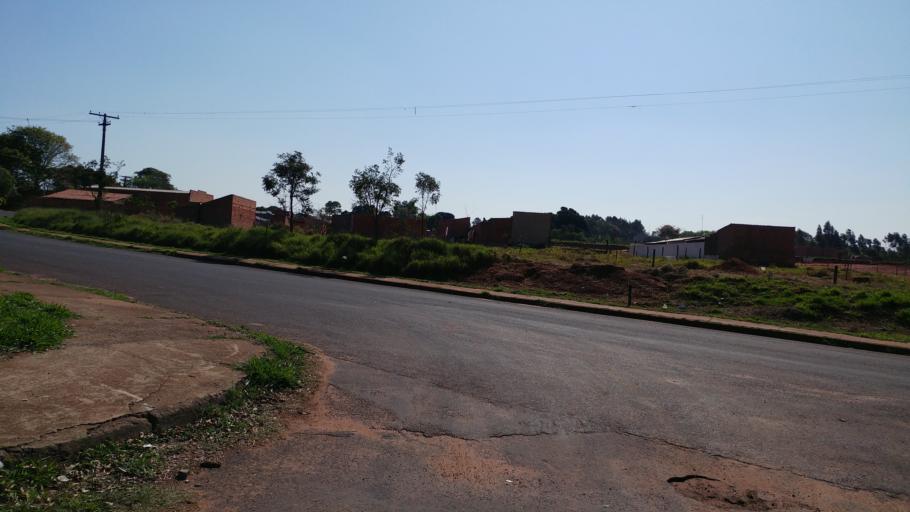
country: BR
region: Sao Paulo
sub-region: Paraguacu Paulista
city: Paraguacu Paulista
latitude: -22.4064
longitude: -50.5641
